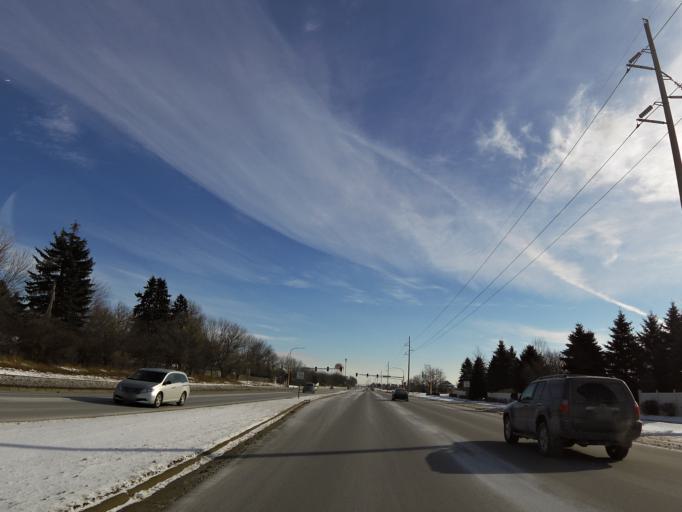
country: US
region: Minnesota
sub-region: Dakota County
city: Rosemount
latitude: 44.7316
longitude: -93.1488
